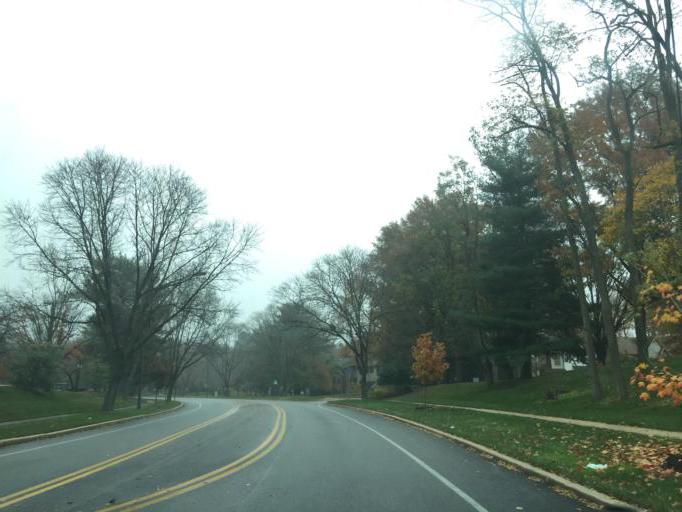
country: US
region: Maryland
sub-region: Howard County
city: Riverside
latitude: 39.1857
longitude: -76.8424
